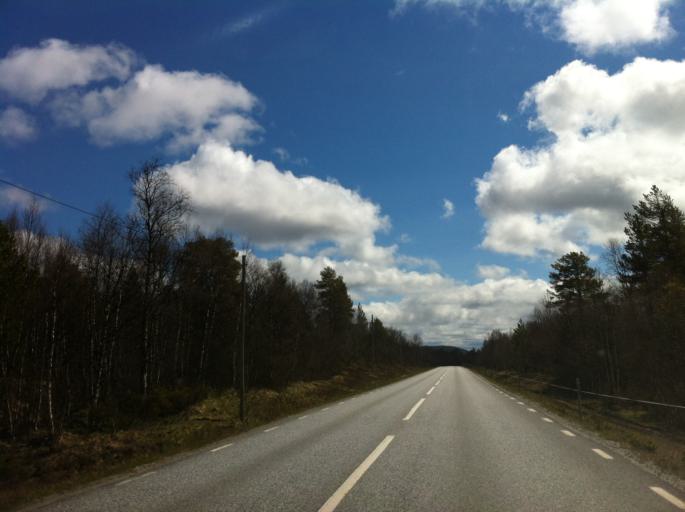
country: NO
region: Sor-Trondelag
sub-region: Tydal
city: Aas
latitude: 62.6139
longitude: 12.4958
